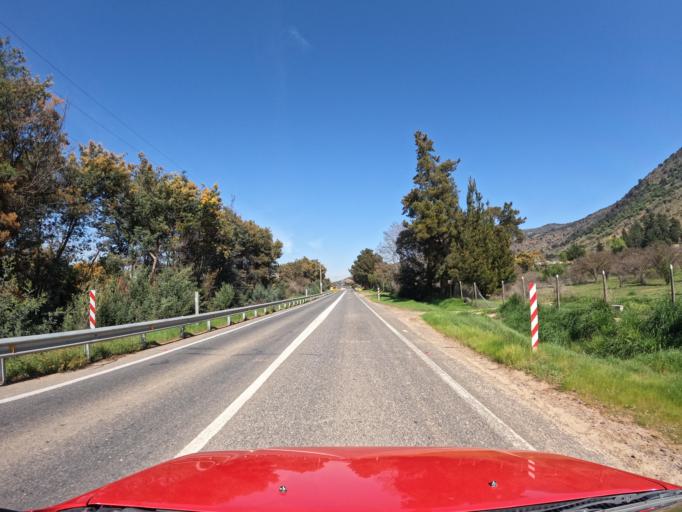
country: CL
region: Maule
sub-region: Provincia de Curico
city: Rauco
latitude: -35.0608
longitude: -71.6181
